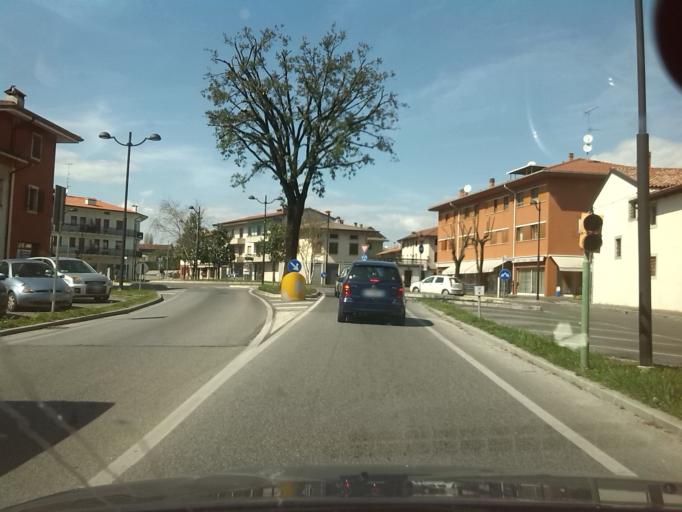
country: IT
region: Friuli Venezia Giulia
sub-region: Provincia di Udine
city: Pagnacco
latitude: 46.1237
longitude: 13.1874
